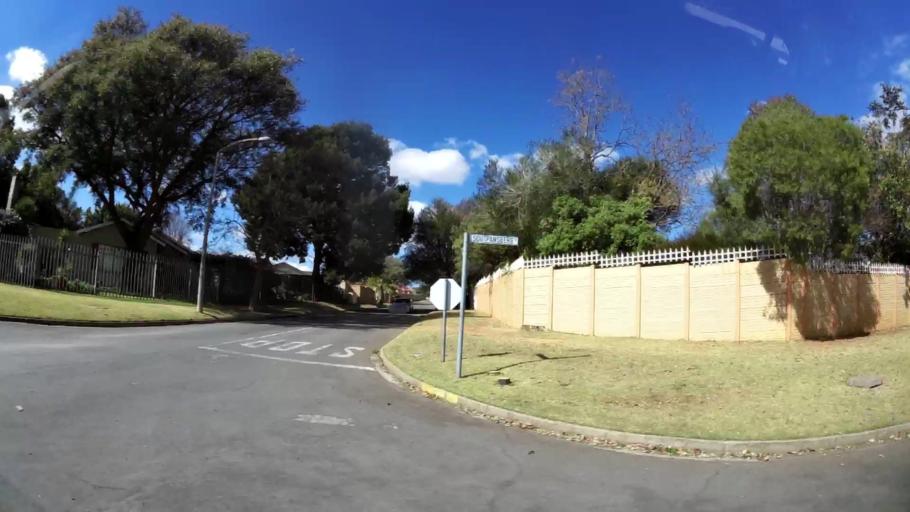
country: ZA
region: Gauteng
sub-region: West Rand District Municipality
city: Krugersdorp
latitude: -26.0894
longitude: 27.7885
